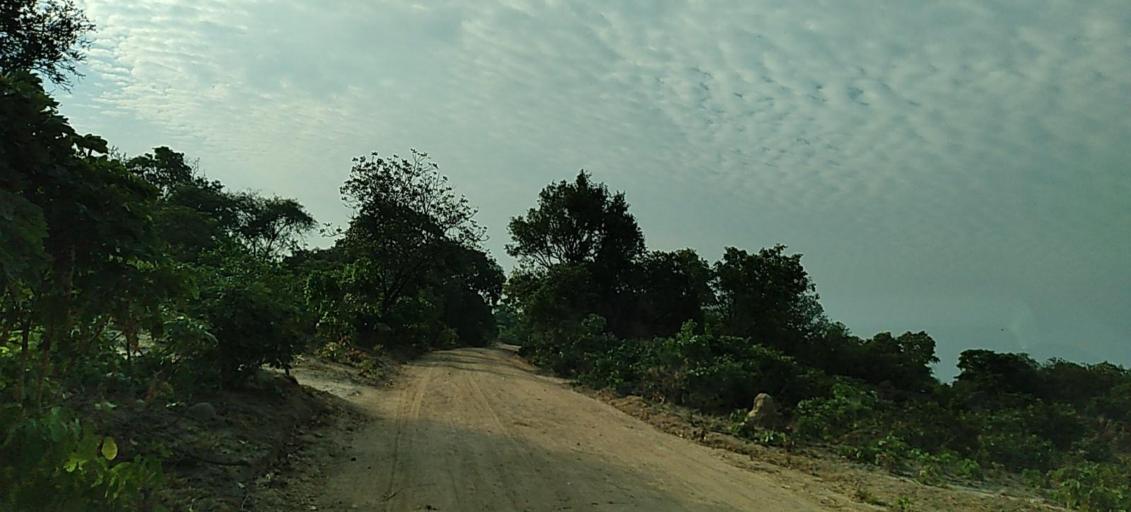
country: ZM
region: Copperbelt
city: Chingola
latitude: -12.8707
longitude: 27.6884
